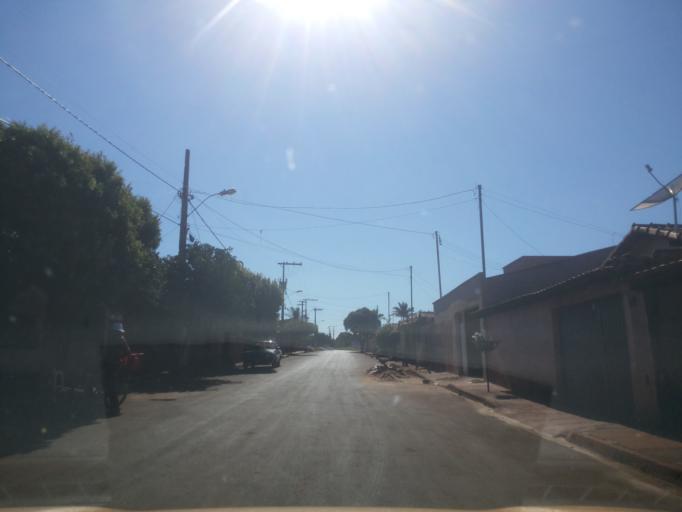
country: BR
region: Minas Gerais
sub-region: Centralina
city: Centralina
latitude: -18.7294
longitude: -49.1974
